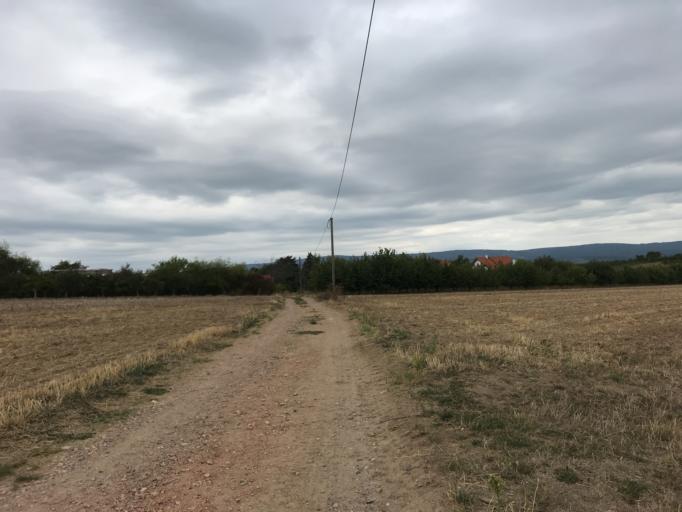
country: DE
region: Rheinland-Pfalz
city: Wackernheim
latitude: 49.9769
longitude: 8.1300
